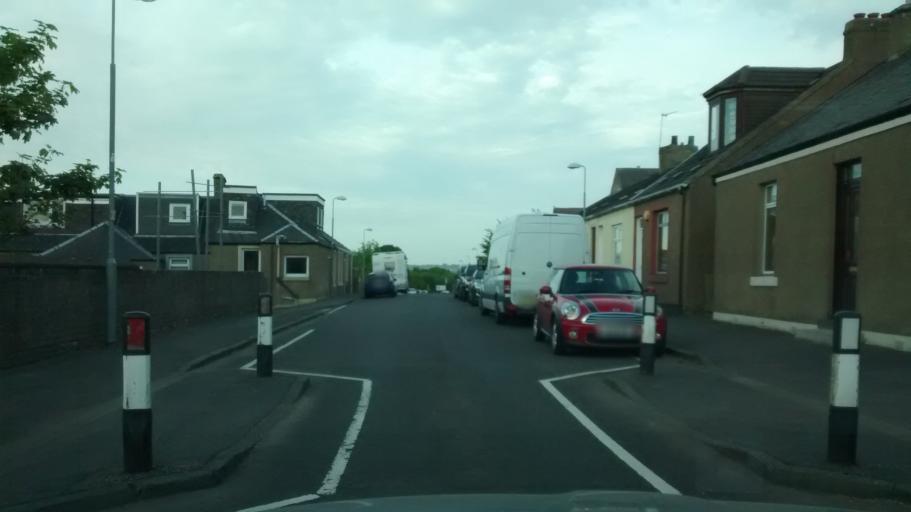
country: GB
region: Scotland
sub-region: West Lothian
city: Armadale
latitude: 55.8965
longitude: -3.7036
